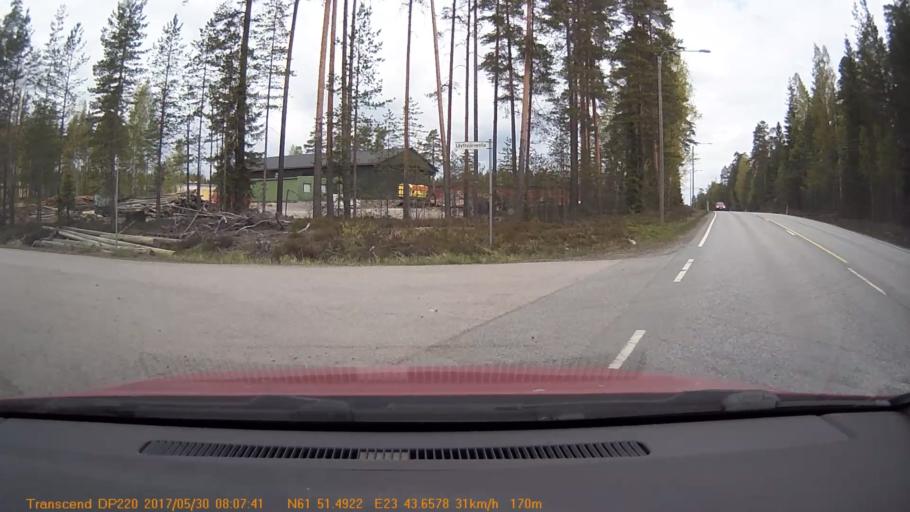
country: FI
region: Pirkanmaa
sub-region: Tampere
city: Kuru
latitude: 61.8580
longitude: 23.7277
